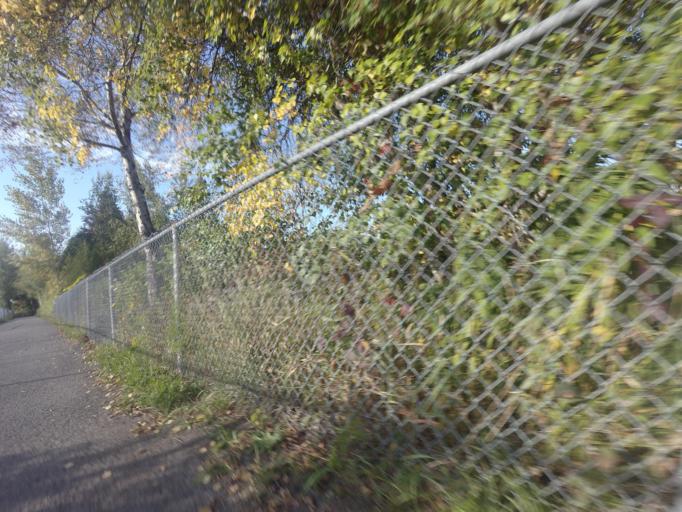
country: CA
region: Quebec
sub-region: Laurentides
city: Saint-Jerome
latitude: 45.7575
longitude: -73.9794
